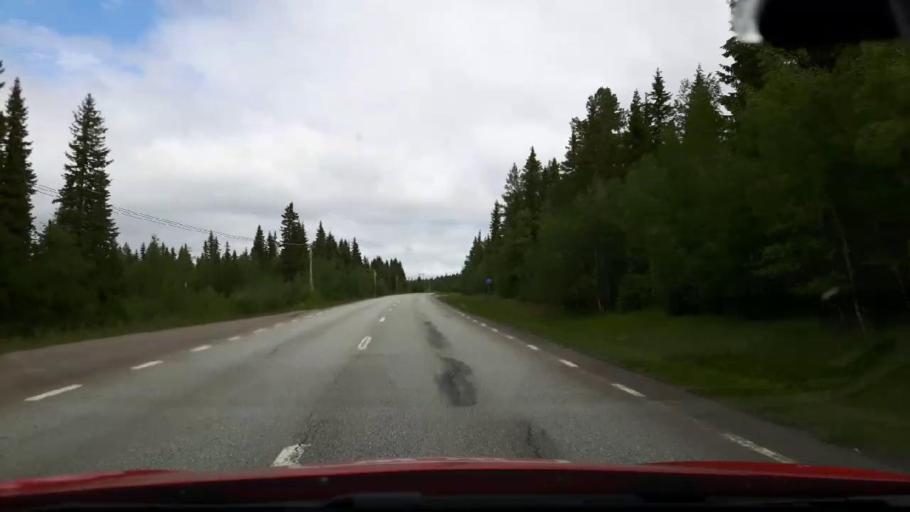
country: SE
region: Jaemtland
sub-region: Krokoms Kommun
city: Krokom
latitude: 63.4677
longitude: 14.4966
